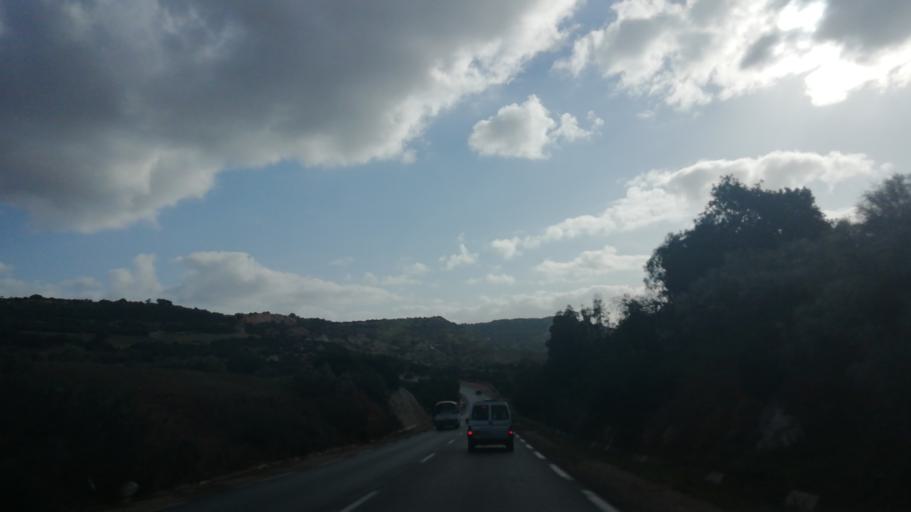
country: DZ
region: Relizane
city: Mazouna
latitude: 36.2376
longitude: 0.5388
